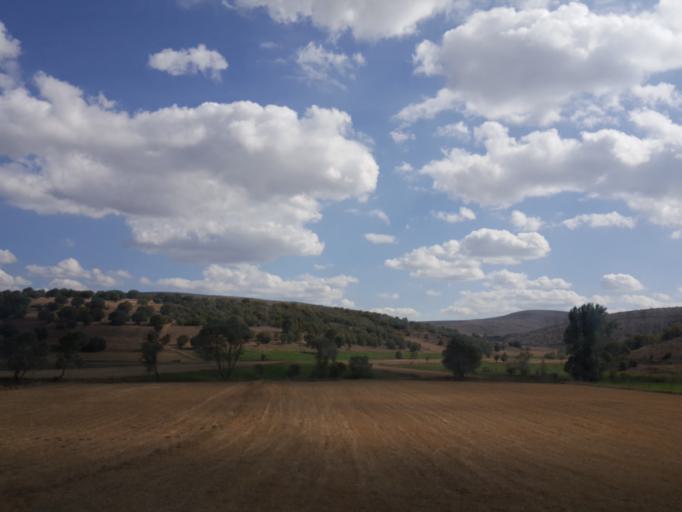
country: TR
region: Tokat
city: Camlibel
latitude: 40.1625
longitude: 36.4188
